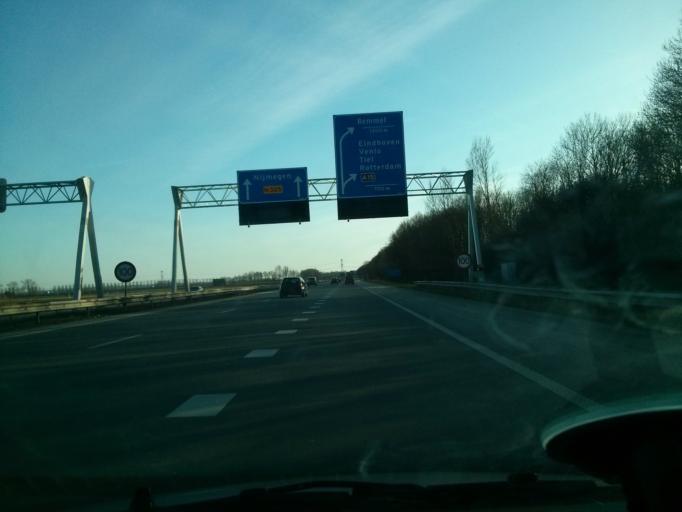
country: NL
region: Gelderland
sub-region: Gemeente Overbetuwe
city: Elst
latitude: 51.9132
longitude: 5.8738
